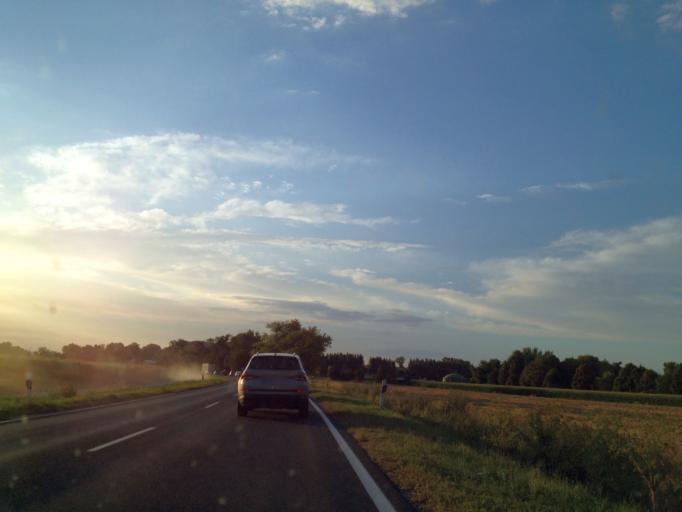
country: HU
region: Gyor-Moson-Sopron
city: Mosonmagyarovar
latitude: 47.8360
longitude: 17.2958
